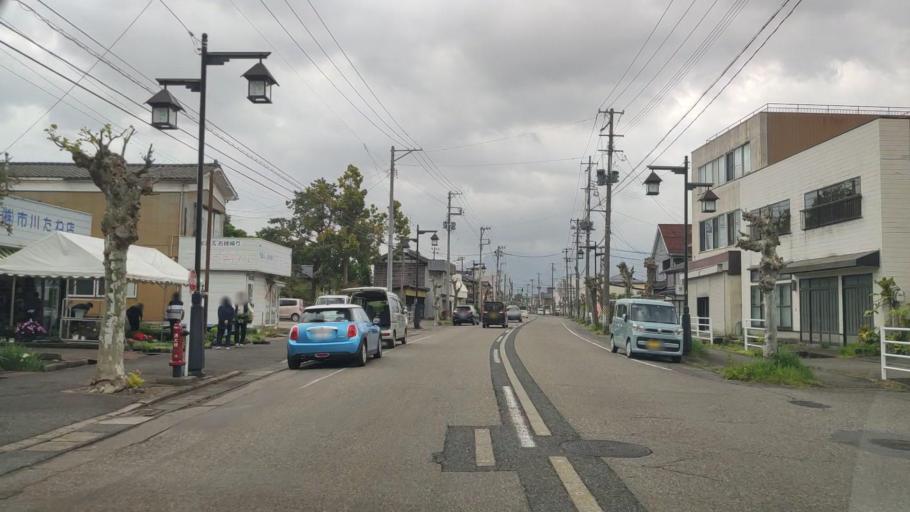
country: JP
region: Niigata
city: Gosen
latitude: 37.7379
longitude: 139.1813
